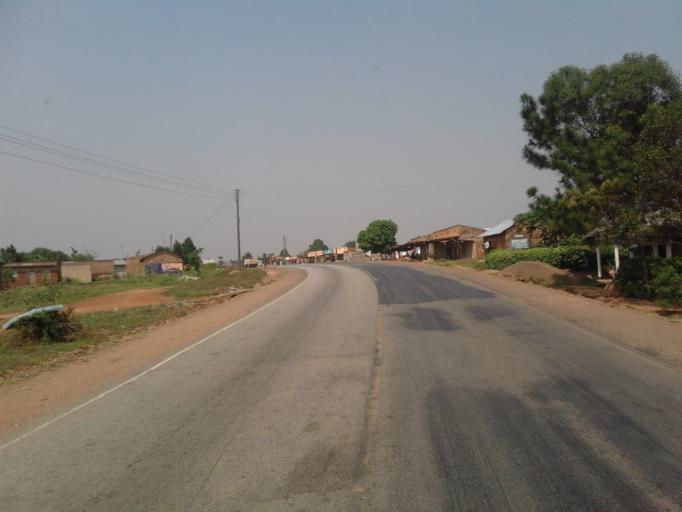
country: UG
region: Eastern Region
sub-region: Iganga District
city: Iganga
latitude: 0.6290
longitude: 33.5200
